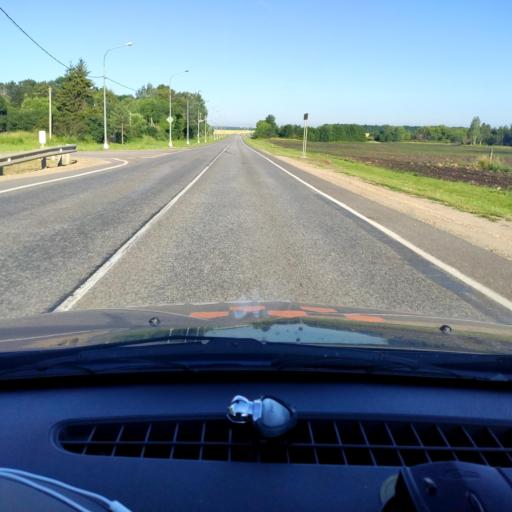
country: RU
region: Orjol
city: Pokrovskoye
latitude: 52.6198
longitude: 36.7397
